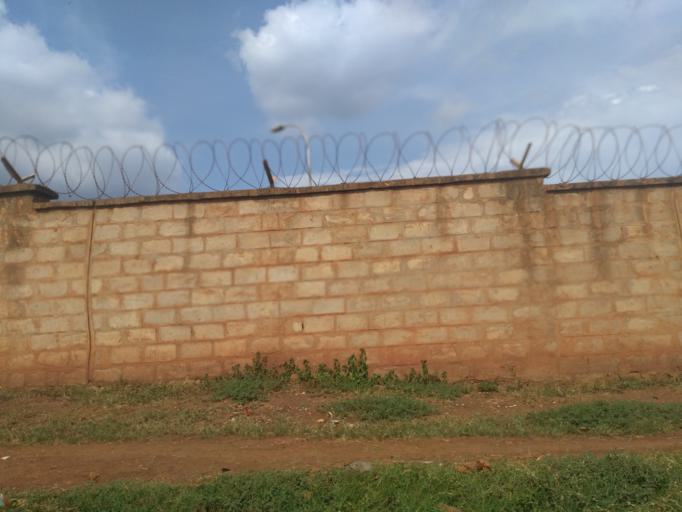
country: UG
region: Eastern Region
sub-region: Jinja District
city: Jinja
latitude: 0.4260
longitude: 33.2199
